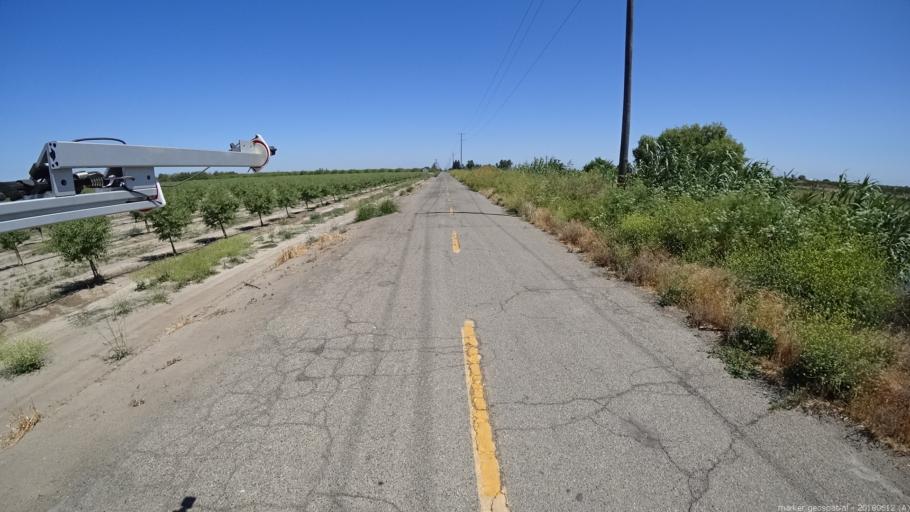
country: US
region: California
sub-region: Madera County
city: Chowchilla
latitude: 37.0121
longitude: -120.3286
